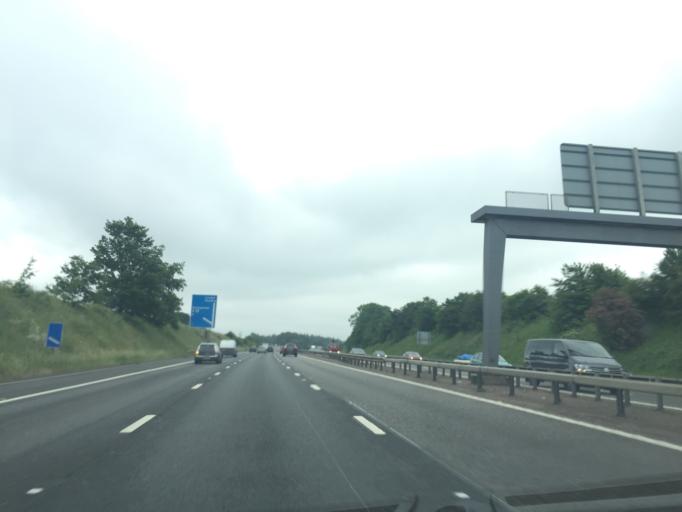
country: GB
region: England
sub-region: Hampshire
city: Basingstoke
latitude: 51.2149
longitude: -1.1680
